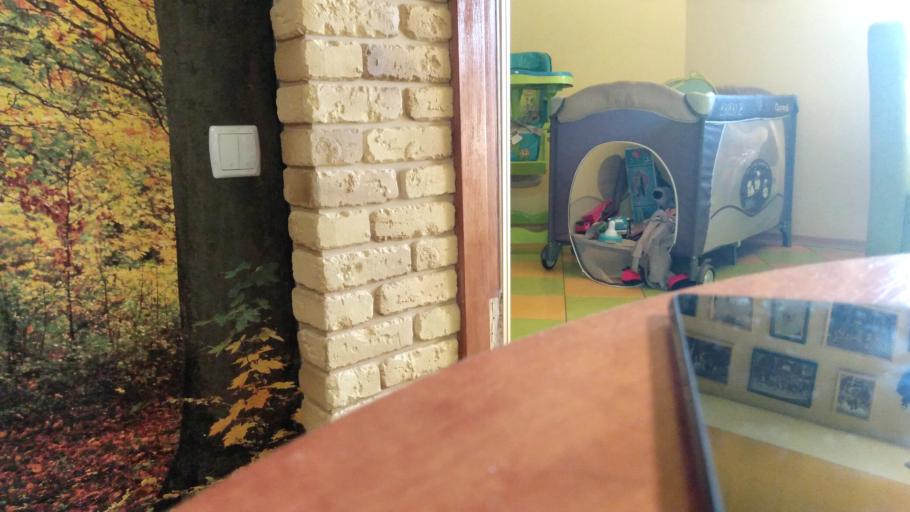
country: RU
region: Tverskaya
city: Bologoye
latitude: 58.0018
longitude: 34.0723
